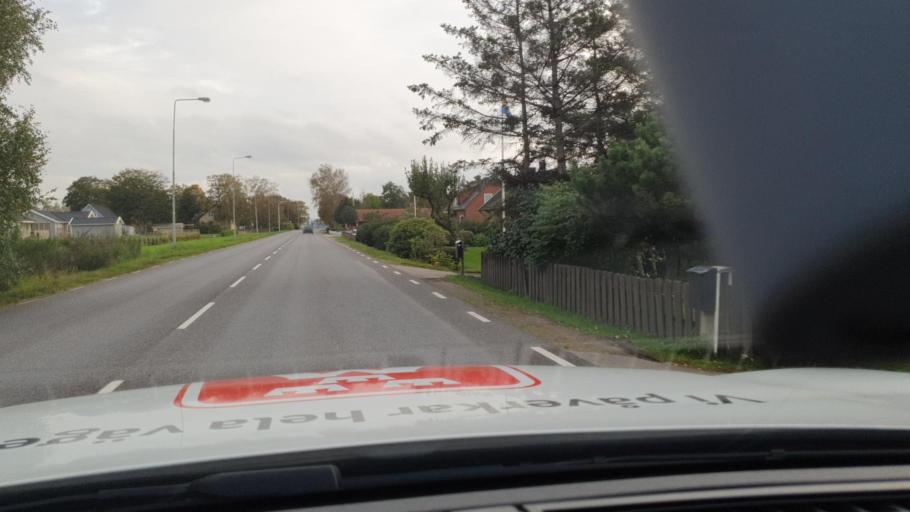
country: SE
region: Halland
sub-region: Laholms Kommun
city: Laholm
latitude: 56.5294
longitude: 13.0517
